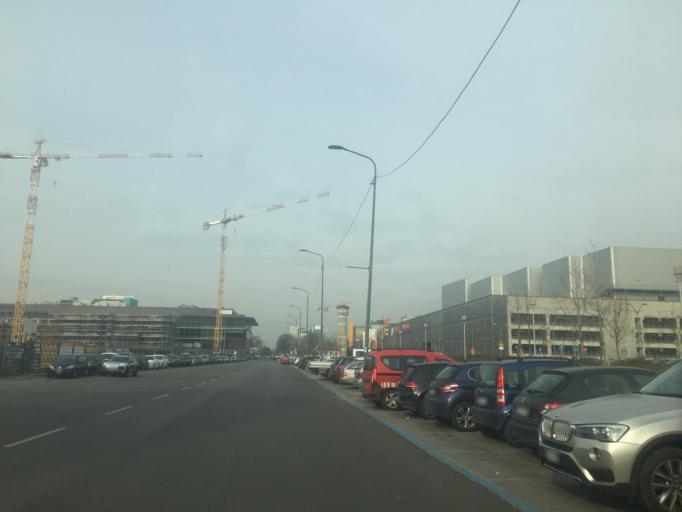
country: IT
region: Lombardy
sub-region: Citta metropolitana di Milano
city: Sesto San Giovanni
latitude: 45.5203
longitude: 9.2176
